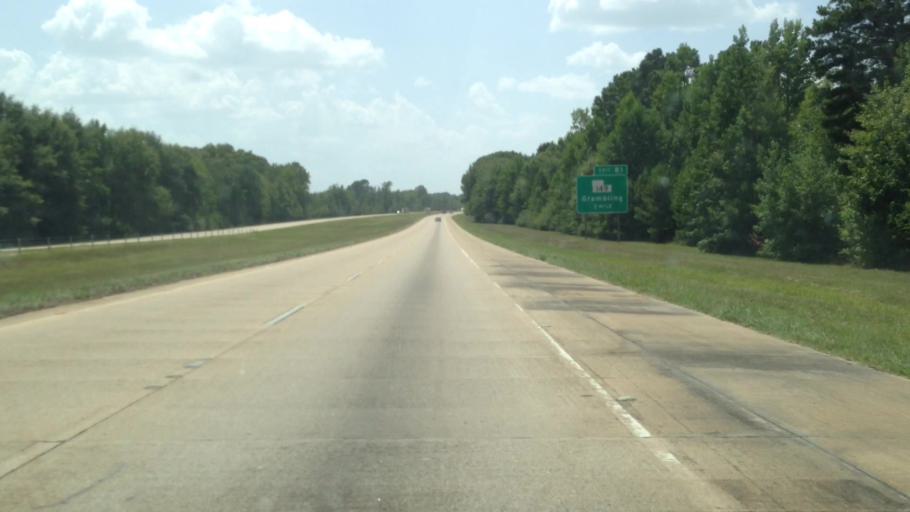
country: US
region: Louisiana
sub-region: Lincoln Parish
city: Grambling
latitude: 32.5407
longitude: -92.6948
